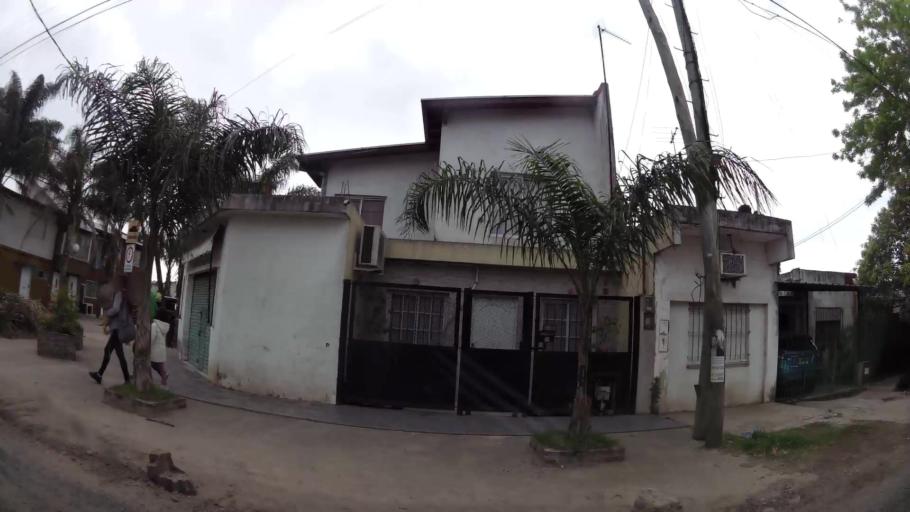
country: AR
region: Buenos Aires
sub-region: Partido de Quilmes
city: Quilmes
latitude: -34.7966
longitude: -58.2696
